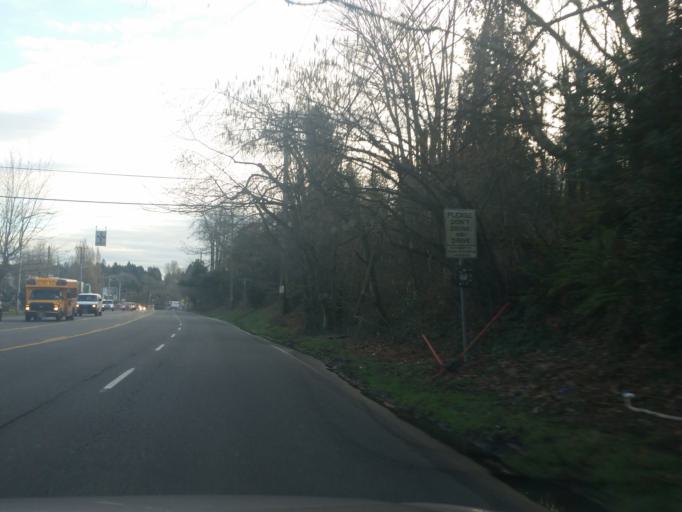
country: US
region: Washington
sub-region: King County
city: Lake Forest Park
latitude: 47.7073
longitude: -122.3018
